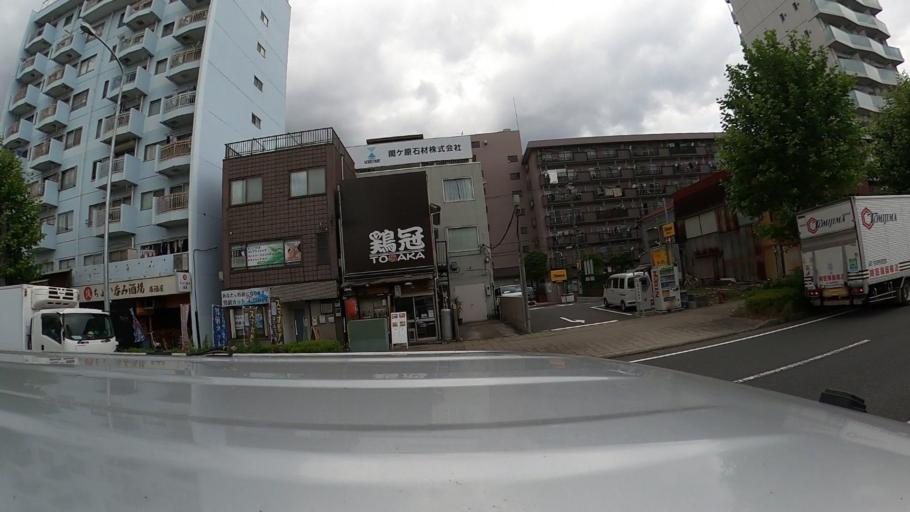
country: JP
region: Kanagawa
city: Yokohama
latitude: 35.4826
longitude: 139.6428
